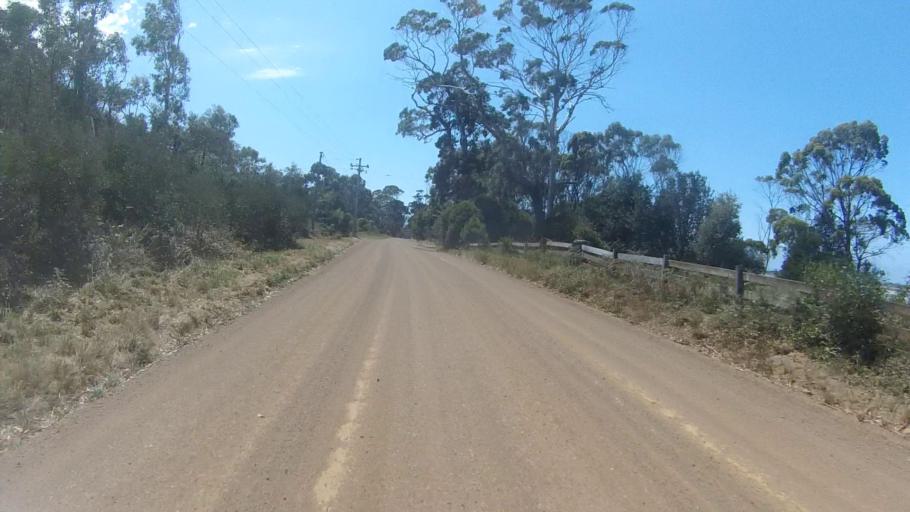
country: AU
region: Tasmania
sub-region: Sorell
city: Sorell
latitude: -42.8364
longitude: 147.8543
